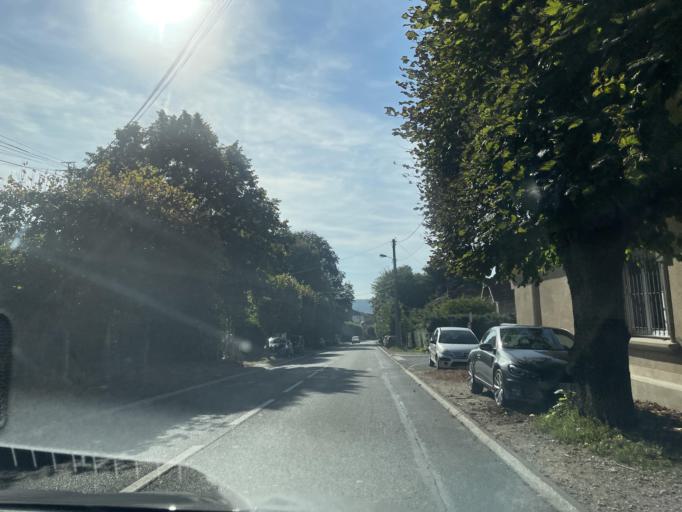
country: FR
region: Ile-de-France
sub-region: Departement de Seine-et-Marne
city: Coulommiers
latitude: 48.8209
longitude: 3.0885
